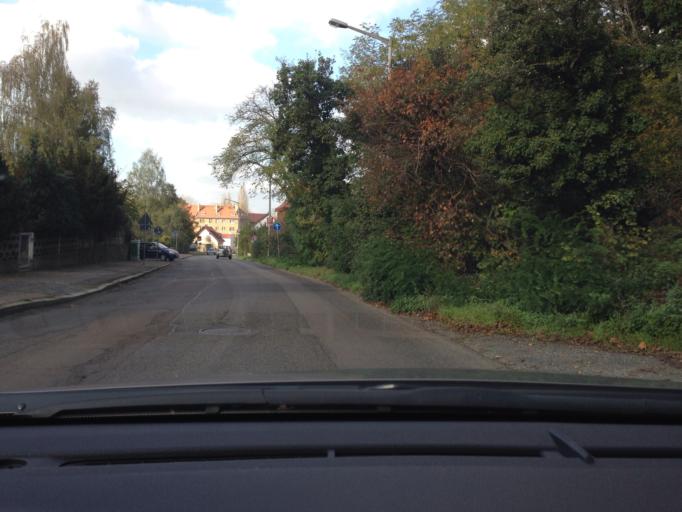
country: DE
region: Saxony
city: Taucha
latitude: 51.3780
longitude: 12.4366
